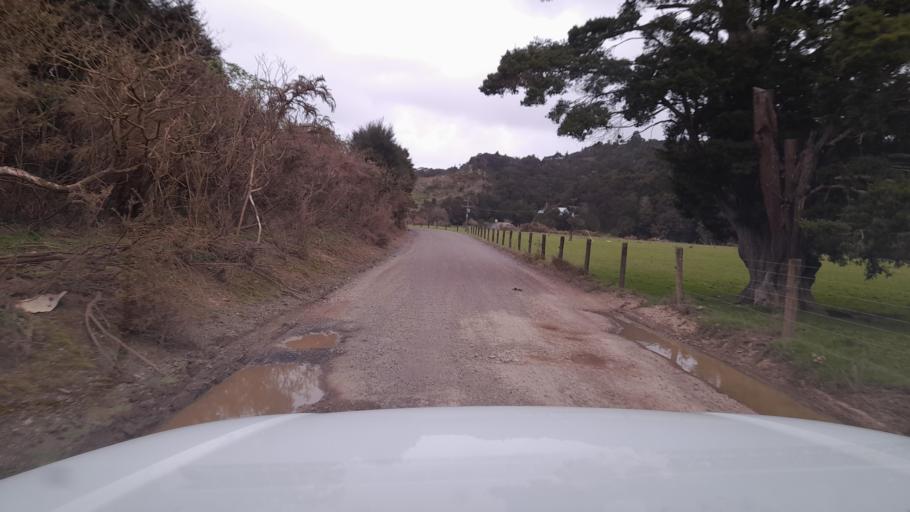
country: NZ
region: Northland
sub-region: Far North District
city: Paihia
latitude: -35.3523
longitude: 174.2266
